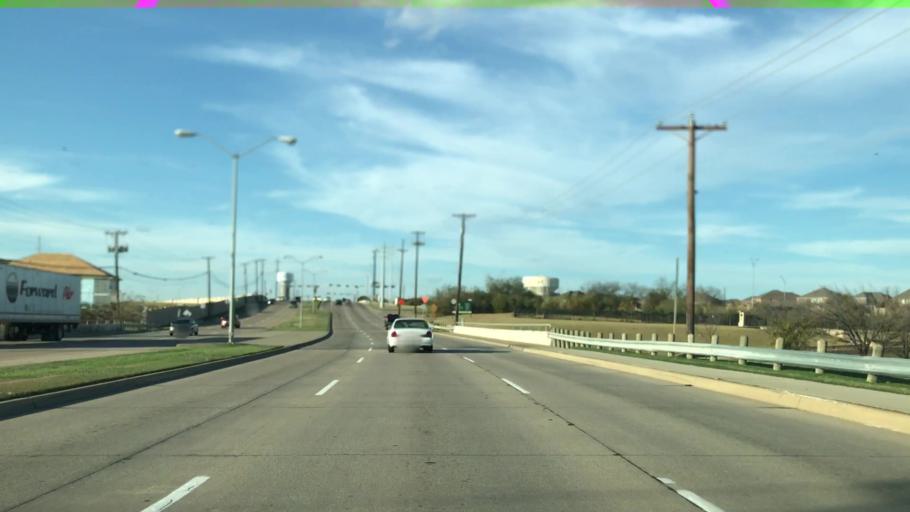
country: US
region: Texas
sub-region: Dallas County
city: Coppell
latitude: 32.9022
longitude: -96.9912
